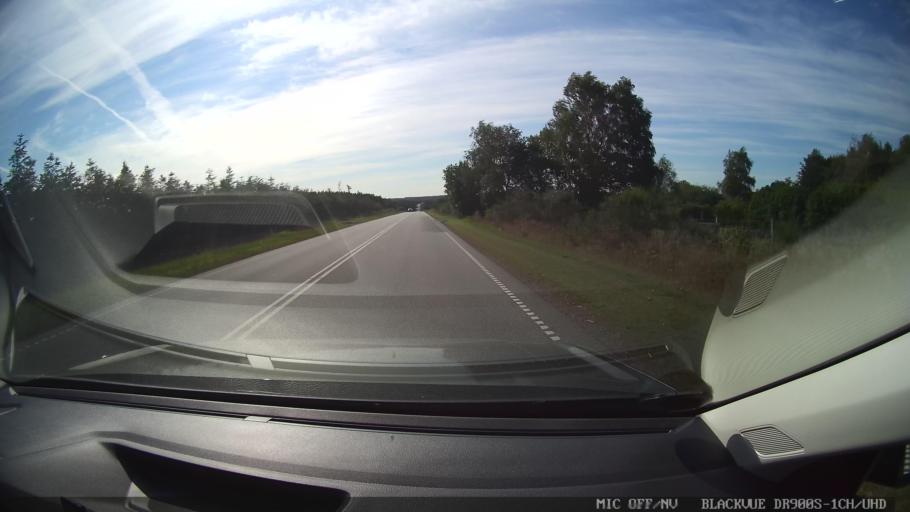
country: DK
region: North Denmark
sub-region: Mariagerfjord Kommune
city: Hadsund
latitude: 56.7643
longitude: 10.0649
